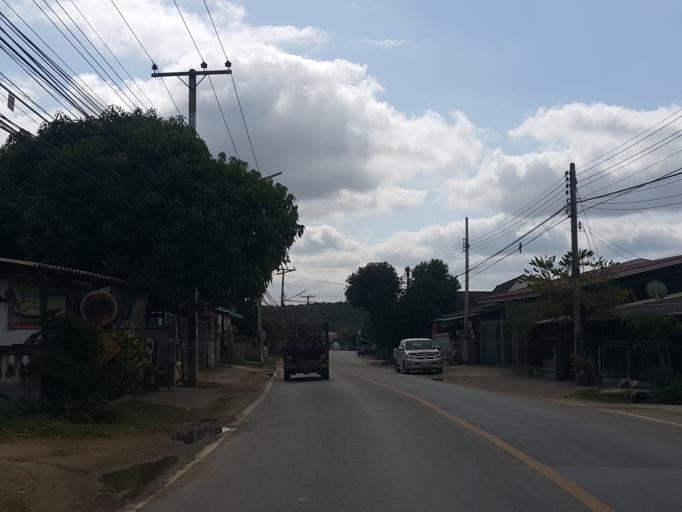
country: TH
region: Lamphun
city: Ban Thi
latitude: 18.6140
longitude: 99.0918
